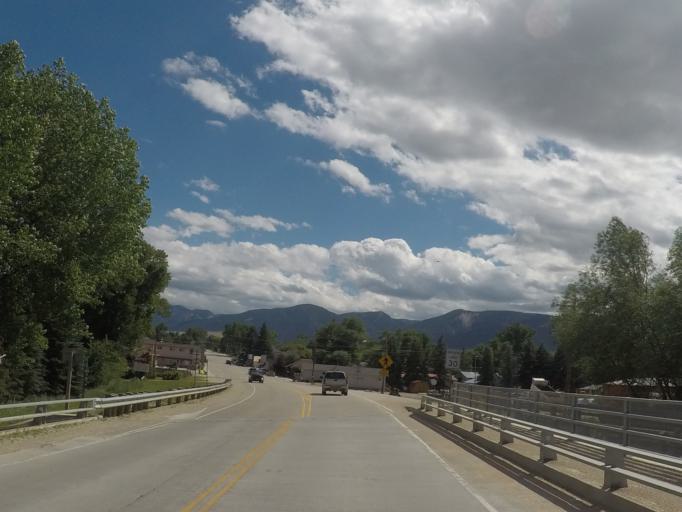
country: US
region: Wyoming
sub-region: Sheridan County
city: Sheridan
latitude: 44.8785
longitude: -107.2626
